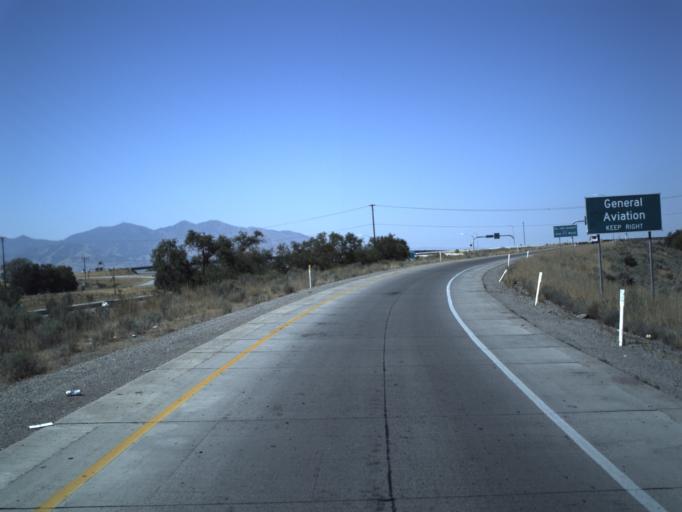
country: US
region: Utah
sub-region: Salt Lake County
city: Salt Lake City
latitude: 40.7669
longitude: -111.9405
